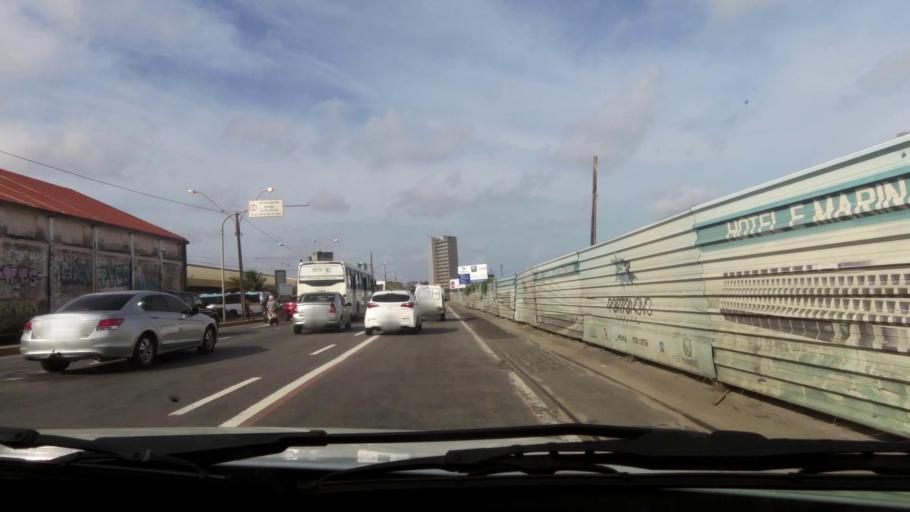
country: BR
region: Pernambuco
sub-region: Recife
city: Recife
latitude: -8.0676
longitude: -34.8740
